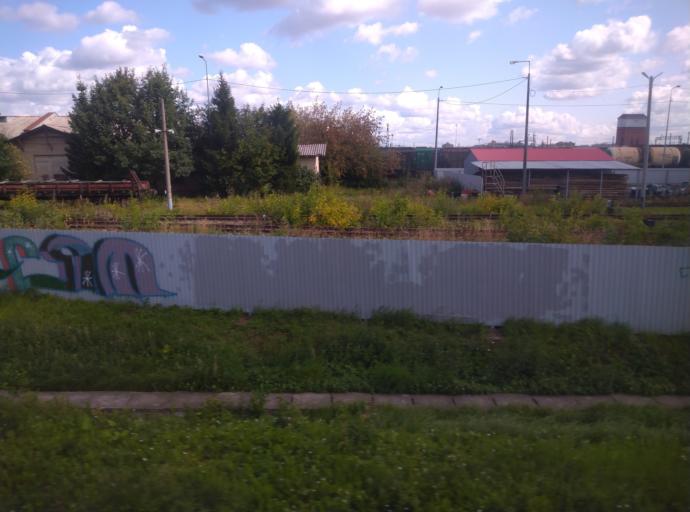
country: RU
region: St.-Petersburg
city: Obukhovo
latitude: 59.8728
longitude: 30.4163
